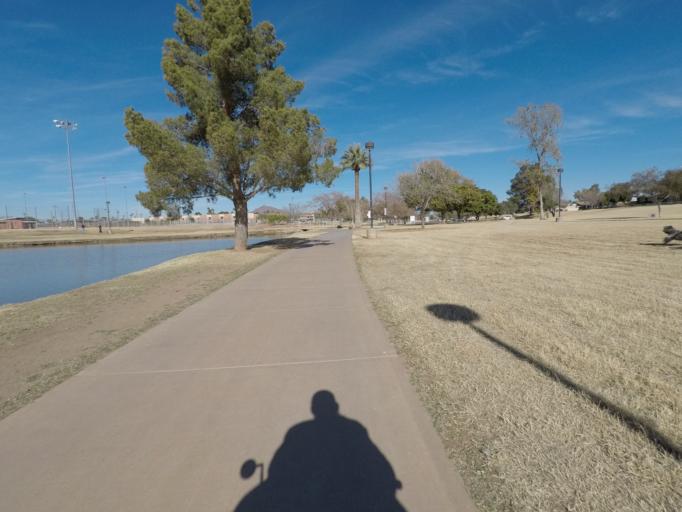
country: US
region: Arizona
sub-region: Maricopa County
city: Tempe
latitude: 33.4559
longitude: -111.9143
